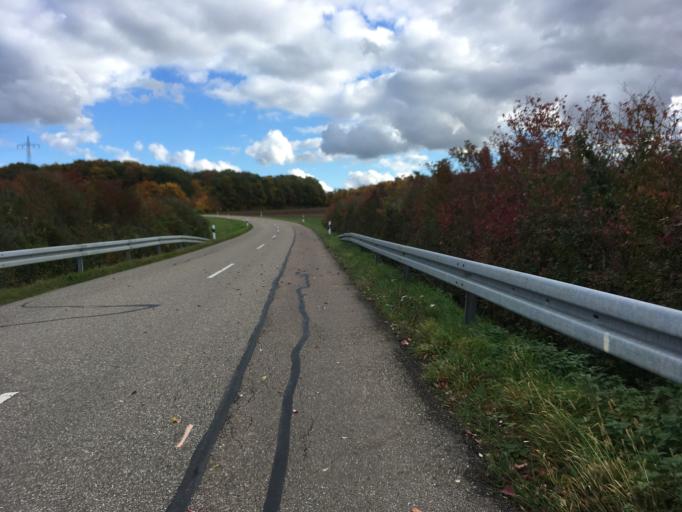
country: DE
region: Baden-Wuerttemberg
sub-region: Regierungsbezirk Stuttgart
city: Untermunkheim
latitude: 49.1875
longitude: 9.7366
